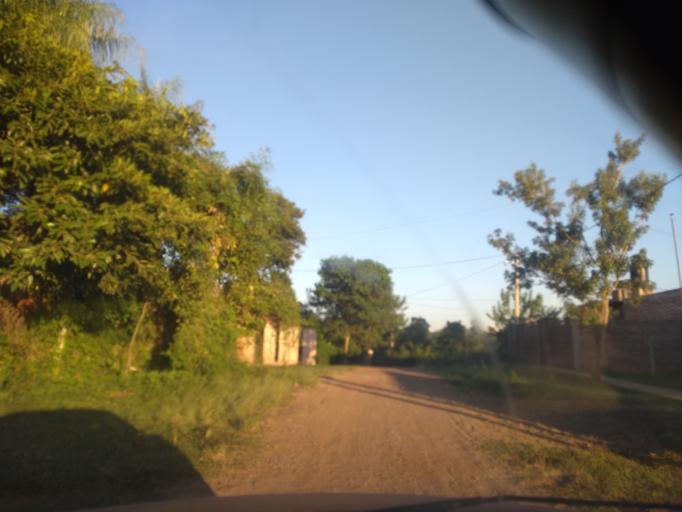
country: AR
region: Chaco
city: Resistencia
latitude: -27.4591
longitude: -58.9686
